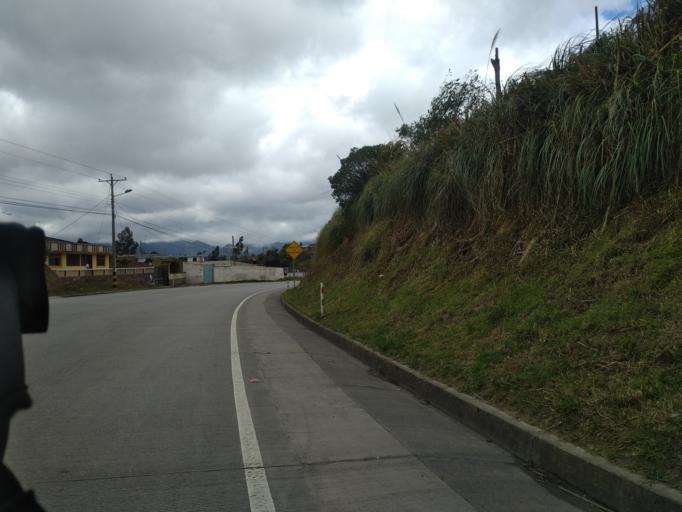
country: EC
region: Loja
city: Loja
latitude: -3.9555
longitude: -79.2445
